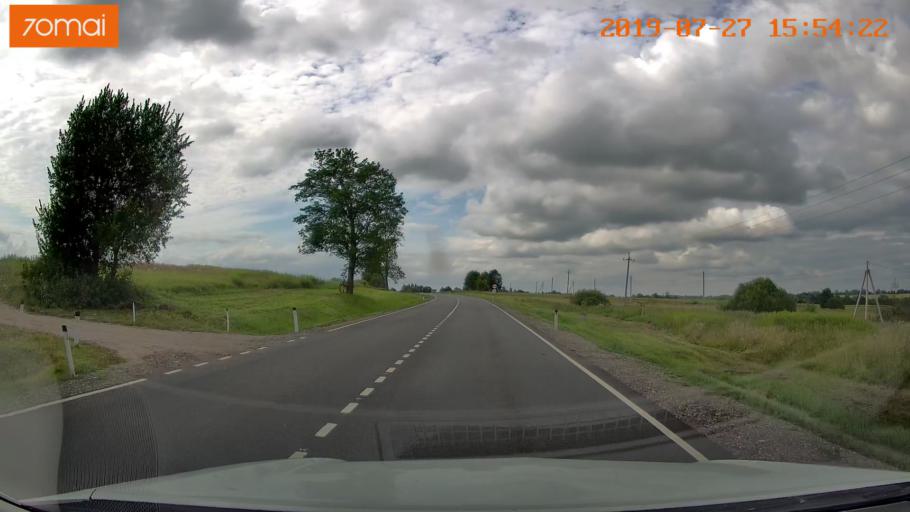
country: RU
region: Kaliningrad
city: Chernyakhovsk
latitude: 54.6072
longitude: 21.9401
